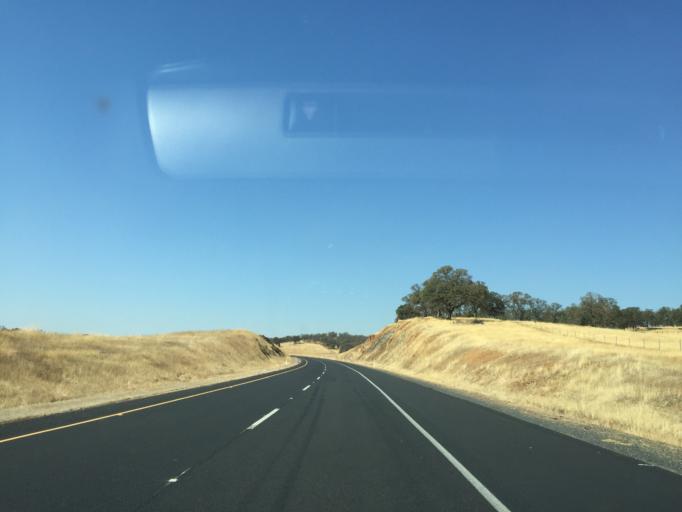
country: US
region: California
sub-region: Calaveras County
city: Copperopolis
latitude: 37.8466
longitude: -120.5529
